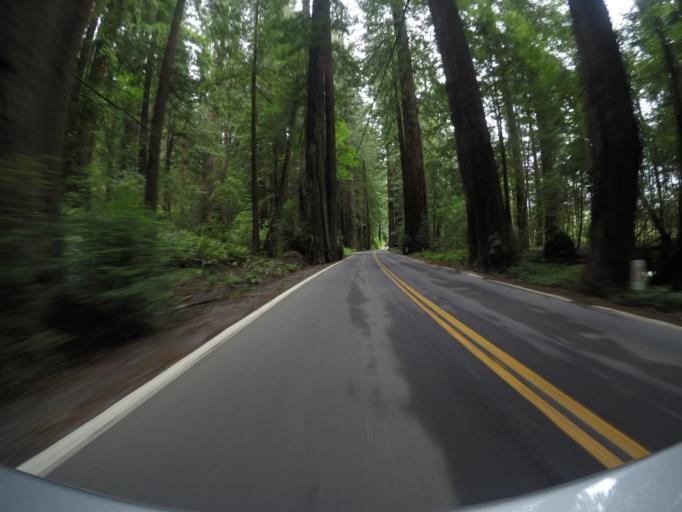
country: US
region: California
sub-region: Humboldt County
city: Rio Dell
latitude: 40.4163
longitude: -123.9649
